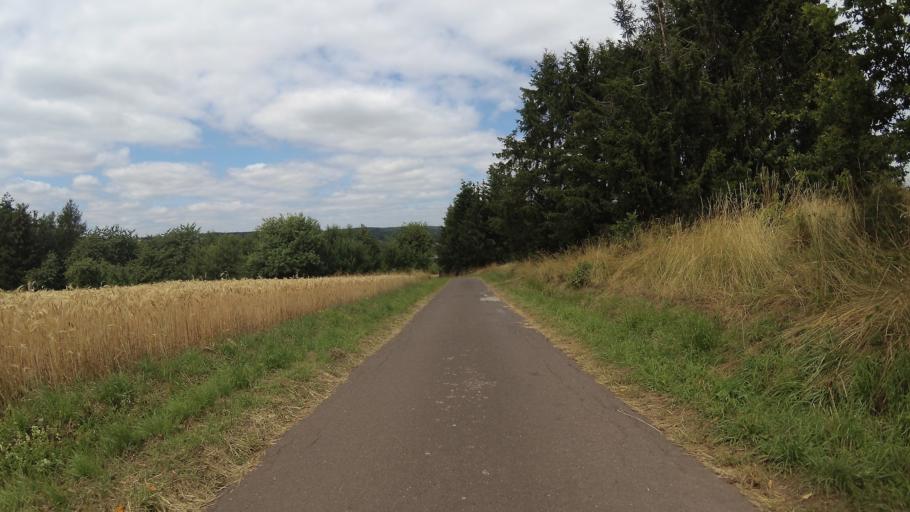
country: DE
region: Saarland
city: Mainzweiler
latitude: 49.4154
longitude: 7.1261
